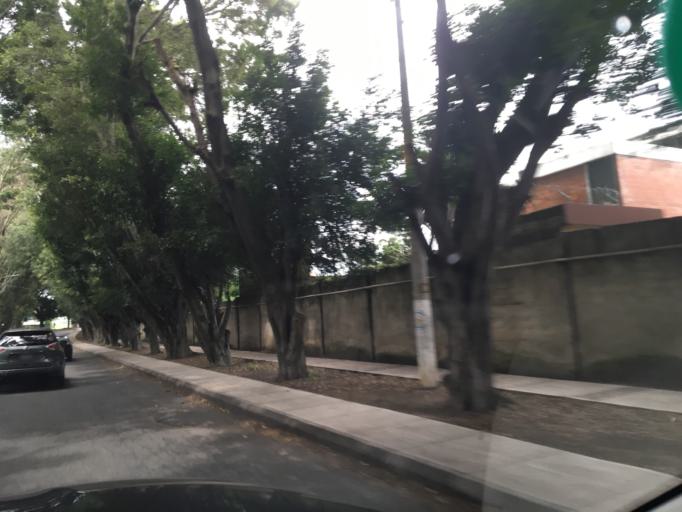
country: GT
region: Guatemala
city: Villa Nueva
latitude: 14.5099
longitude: -90.5817
